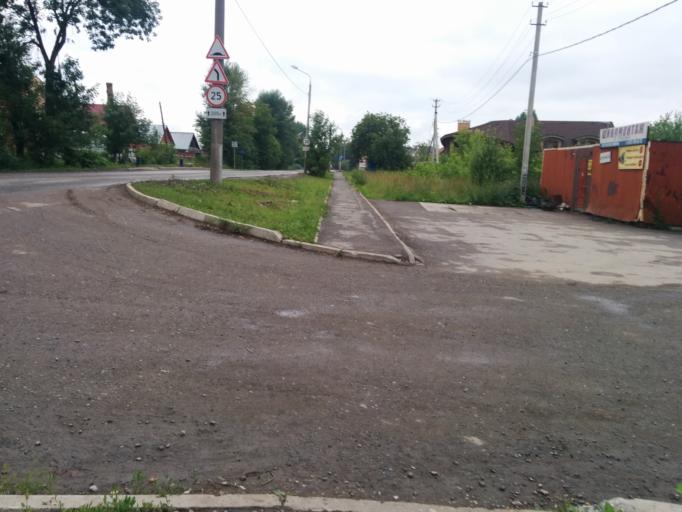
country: RU
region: Perm
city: Perm
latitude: 57.9852
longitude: 56.3045
